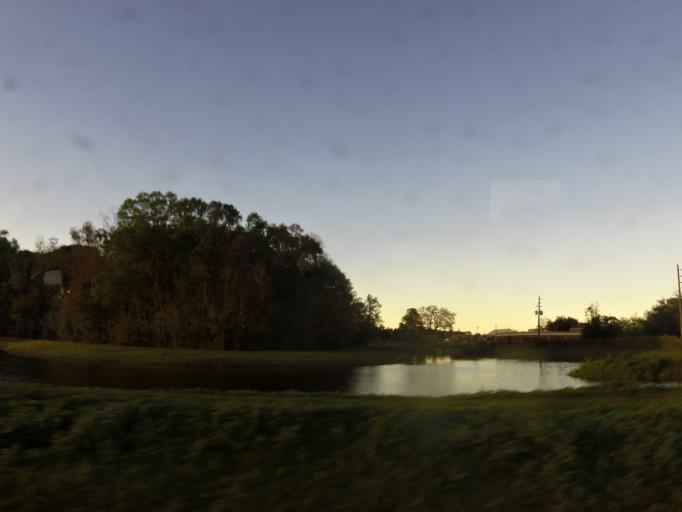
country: US
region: Florida
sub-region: Duval County
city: Jacksonville
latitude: 30.3403
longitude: -81.7273
